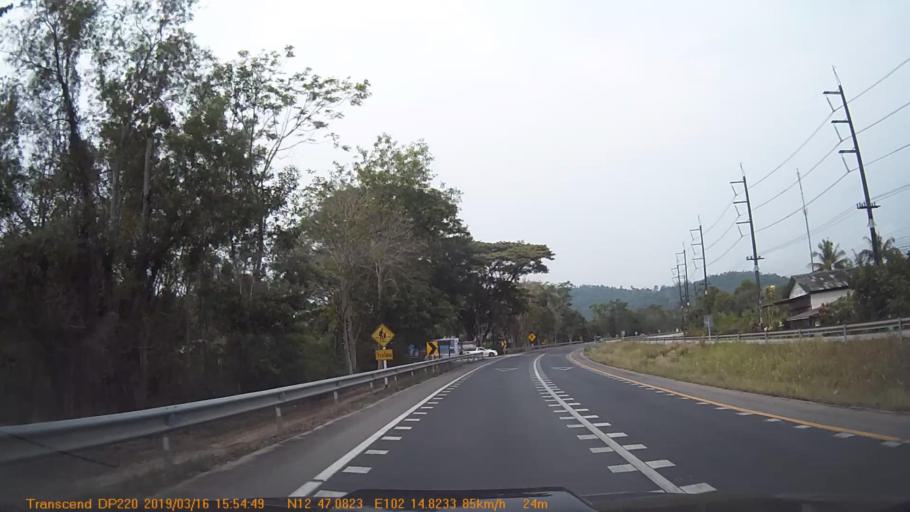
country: TH
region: Chanthaburi
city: Pong Nam Ron
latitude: 12.7851
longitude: 102.2471
